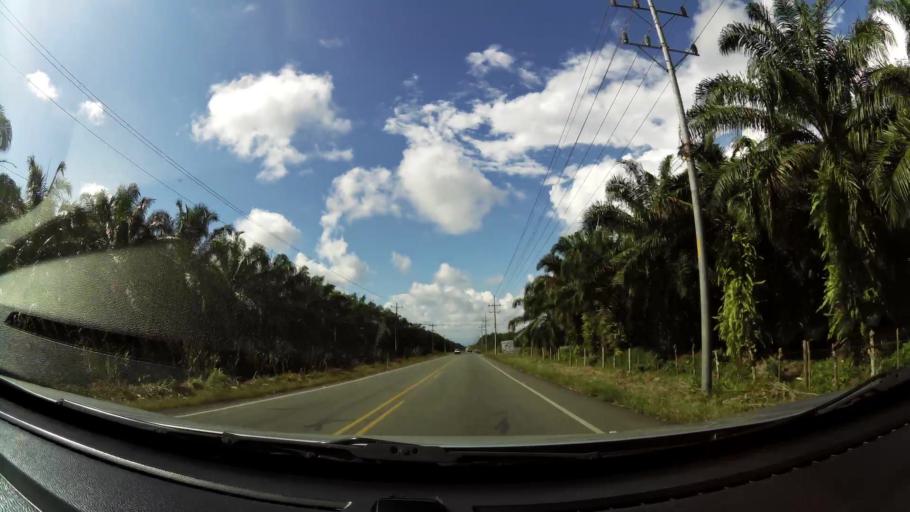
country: CR
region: Puntarenas
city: Quepos
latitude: 9.4689
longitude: -84.1889
